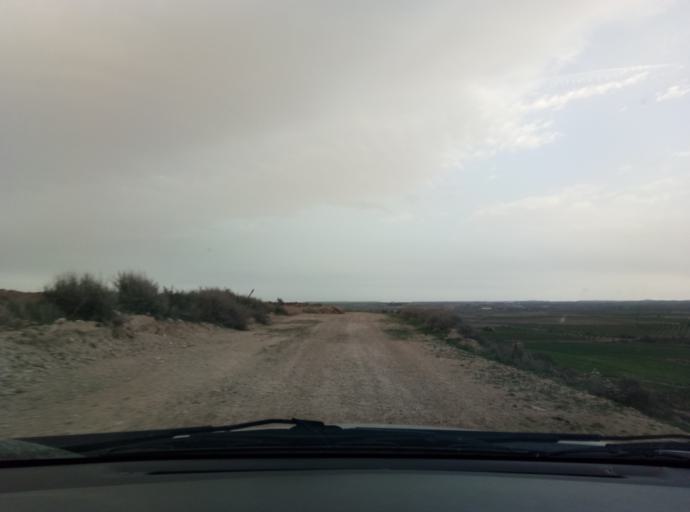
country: ES
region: Catalonia
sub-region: Provincia de Lleida
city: Verdu
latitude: 41.6106
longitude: 1.0987
